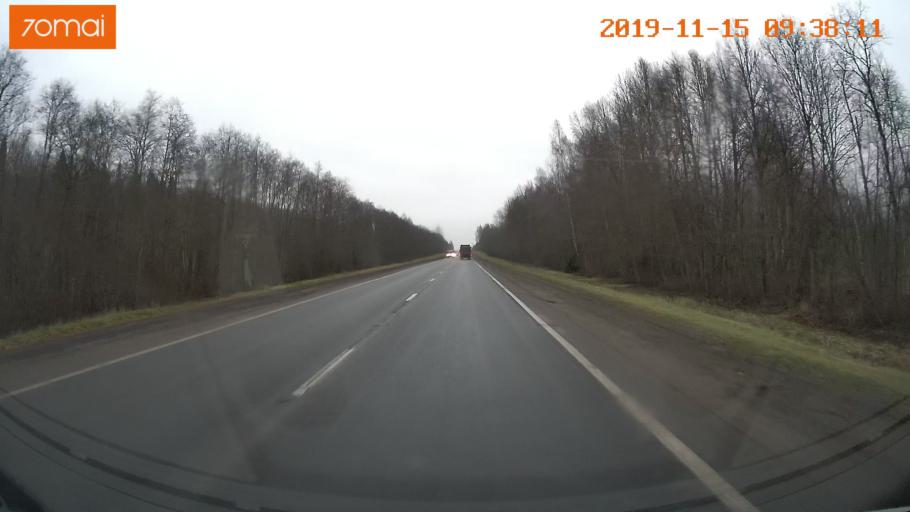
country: RU
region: Vologda
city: Sheksna
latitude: 59.2342
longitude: 38.4508
